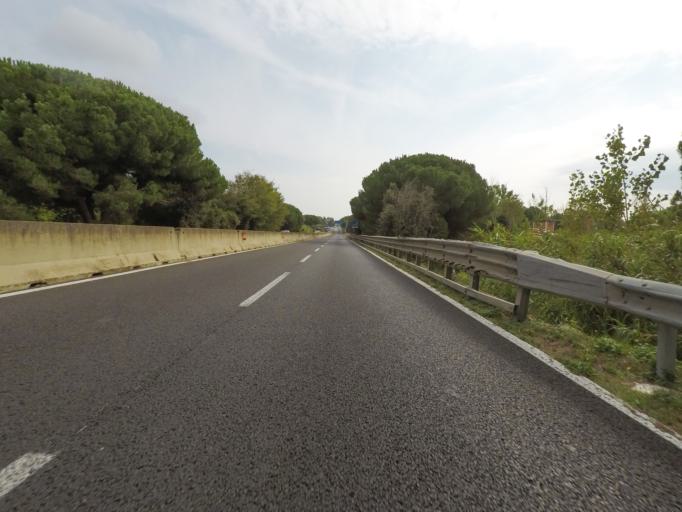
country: IT
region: Tuscany
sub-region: Provincia di Grosseto
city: Orbetello Scalo
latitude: 42.4765
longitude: 11.2317
